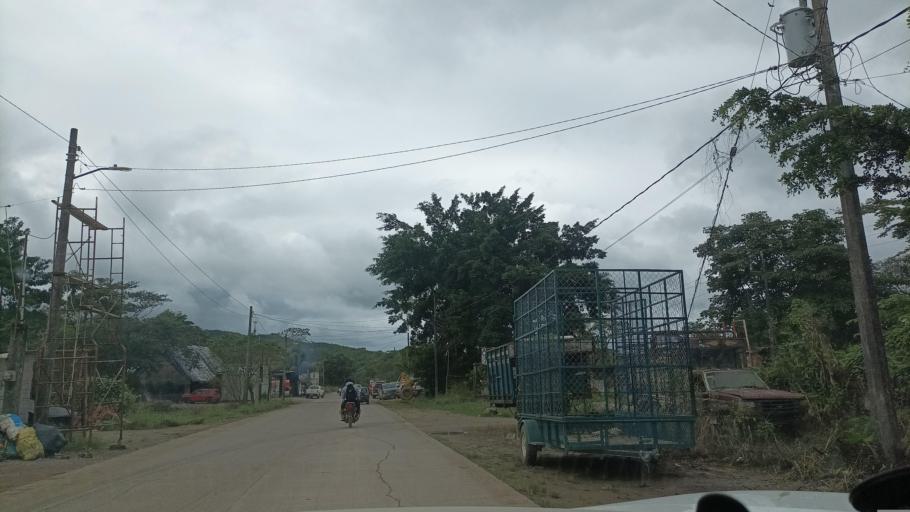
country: MX
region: Veracruz
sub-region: Uxpanapa
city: Poblado 10
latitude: 17.2782
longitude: -94.4572
